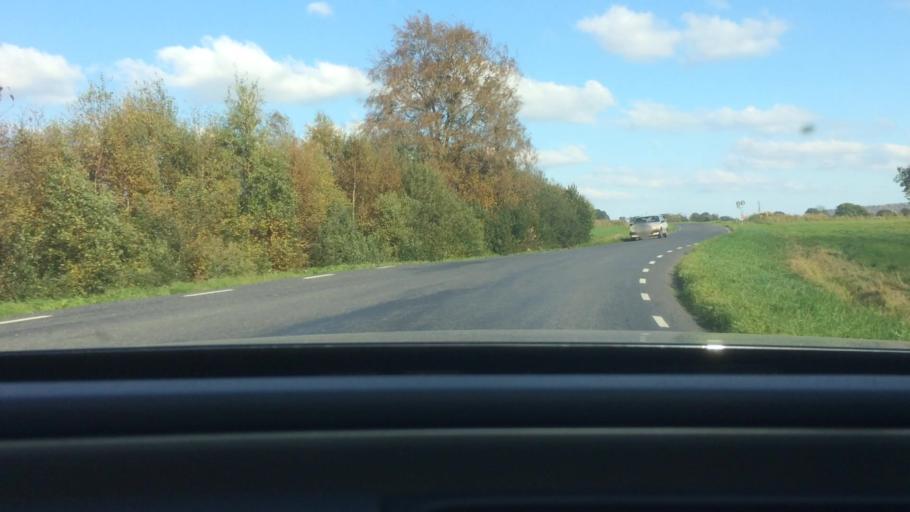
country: SE
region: Vaestra Goetaland
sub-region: Falkopings Kommun
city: Falkoeping
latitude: 58.1385
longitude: 13.5304
